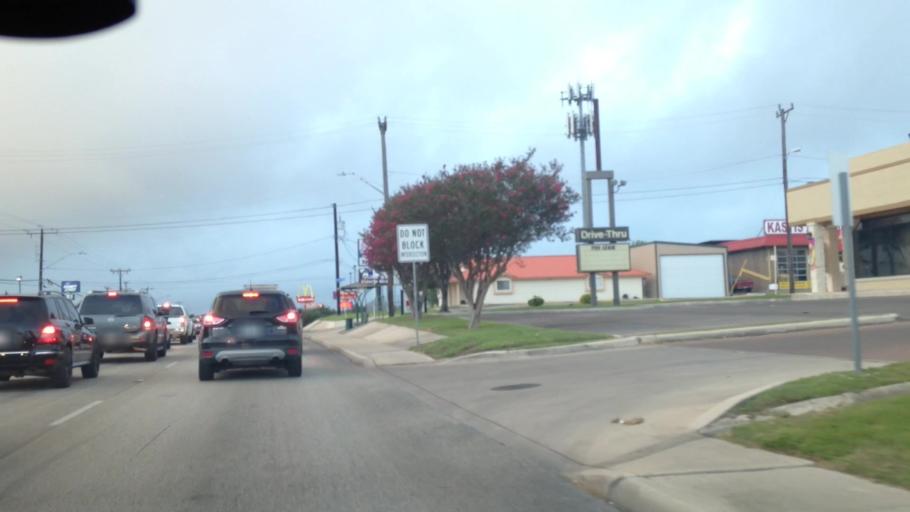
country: US
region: Texas
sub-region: Bexar County
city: Live Oak
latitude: 29.5699
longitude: -98.3831
